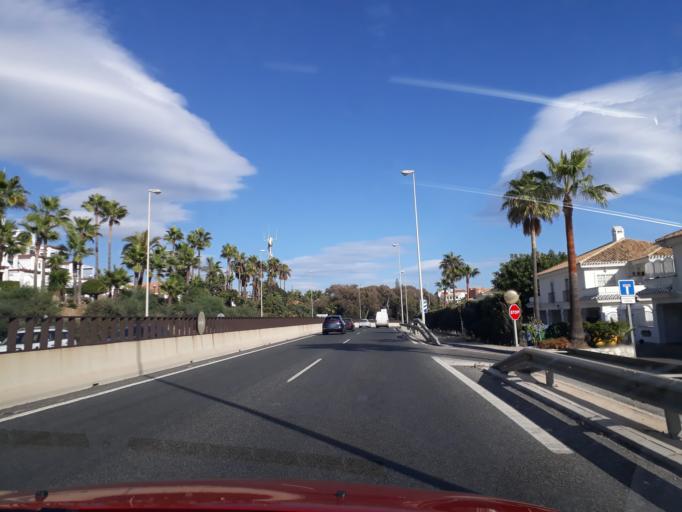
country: ES
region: Andalusia
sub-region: Provincia de Malaga
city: Fuengirola
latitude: 36.5077
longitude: -4.6480
